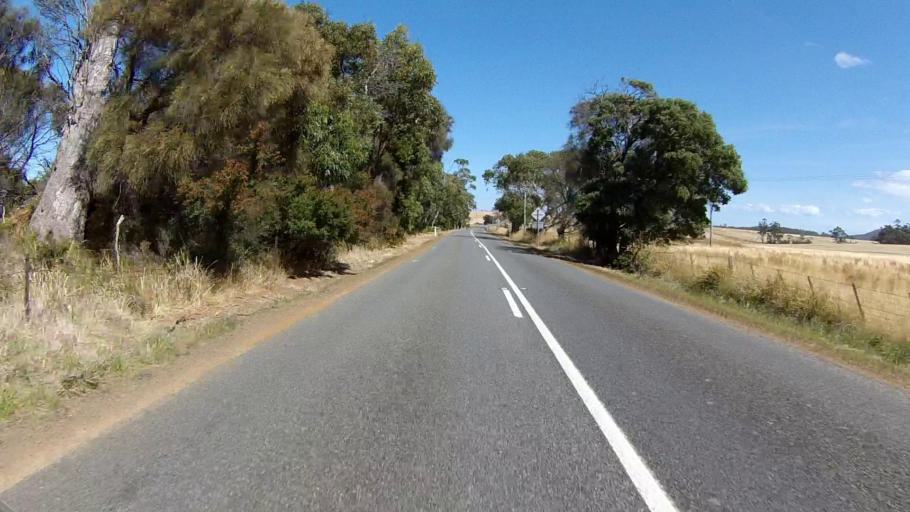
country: AU
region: Tasmania
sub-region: Sorell
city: Sorell
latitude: -42.2435
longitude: 148.0114
